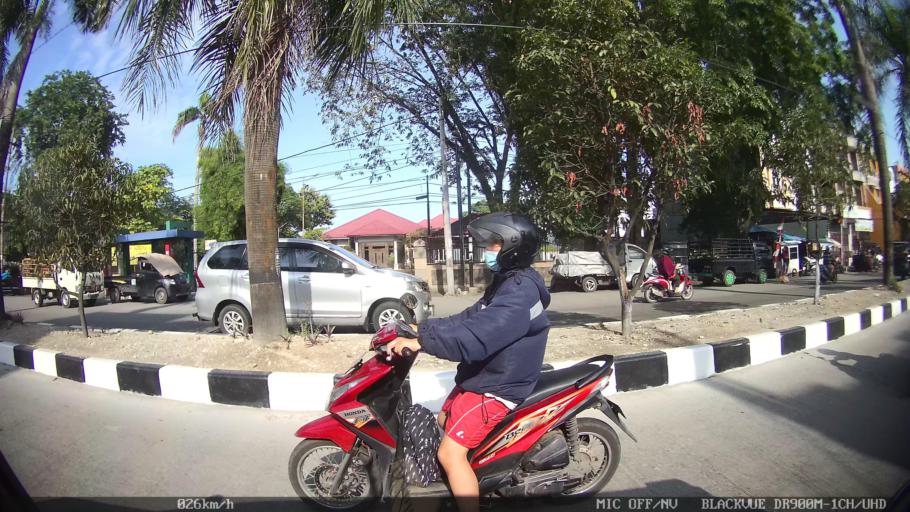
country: ID
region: North Sumatra
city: Medan
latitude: 3.5933
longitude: 98.6441
